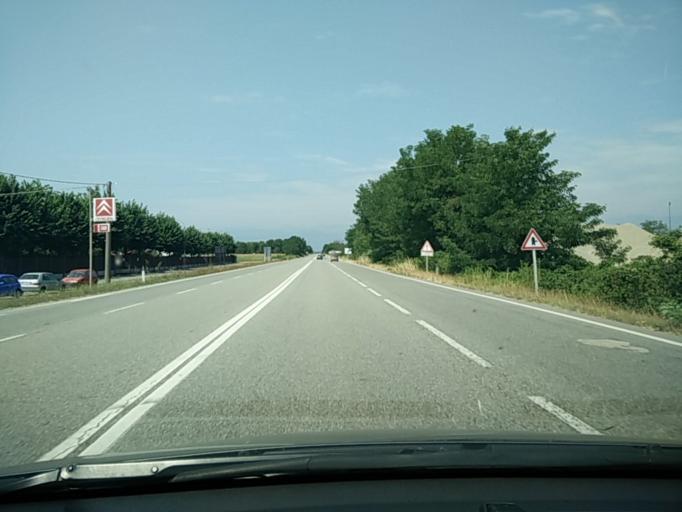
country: IT
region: Piedmont
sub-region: Provincia di Torino
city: Volpiano
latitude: 45.1879
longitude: 7.7683
